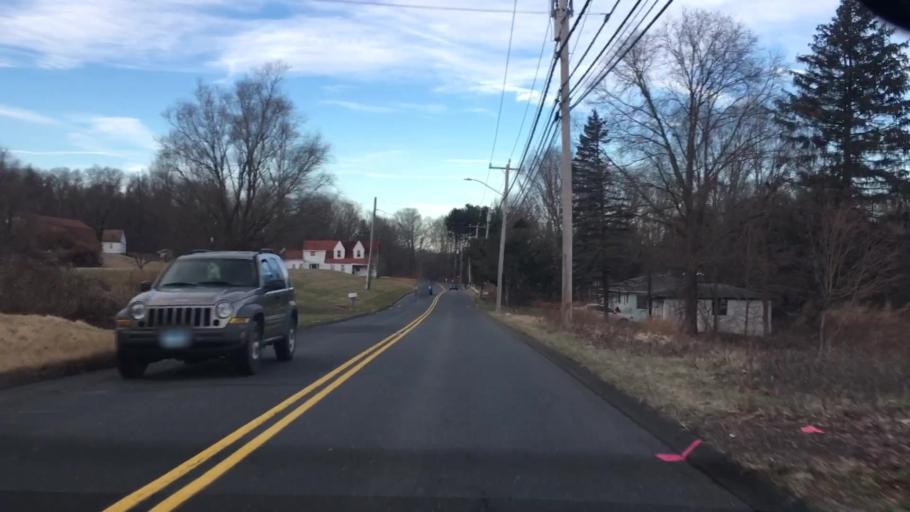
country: US
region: Connecticut
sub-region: New Haven County
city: Cheshire Village
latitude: 41.5423
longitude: -72.9280
